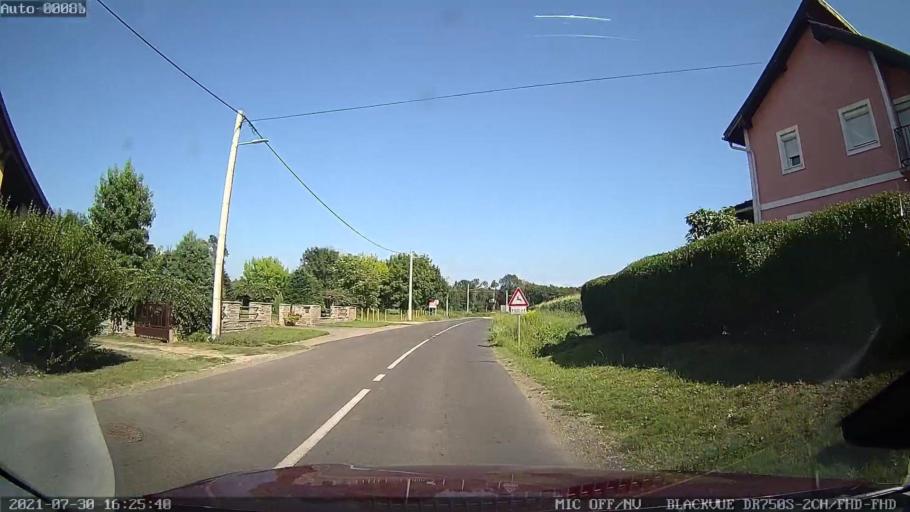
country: HR
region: Medimurska
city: Kursanec
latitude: 46.2816
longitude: 16.4146
